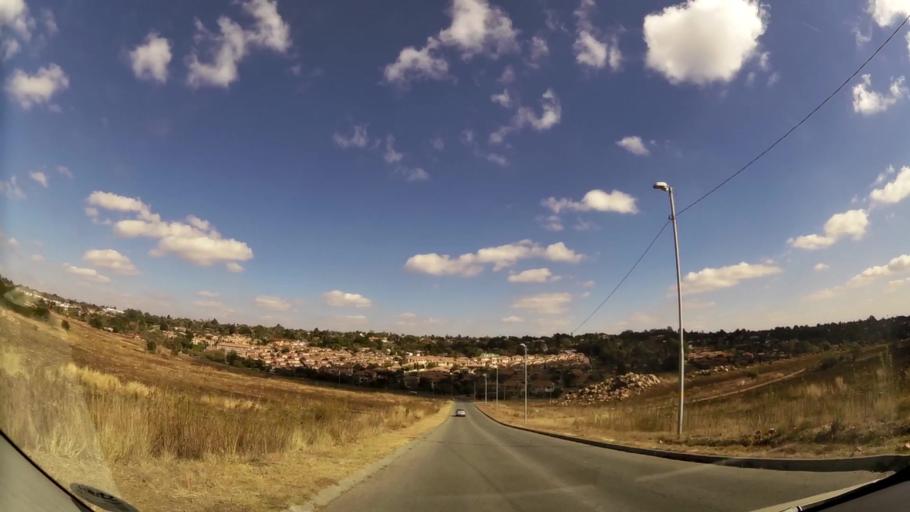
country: ZA
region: Gauteng
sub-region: West Rand District Municipality
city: Krugersdorp
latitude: -26.0902
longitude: 27.8019
